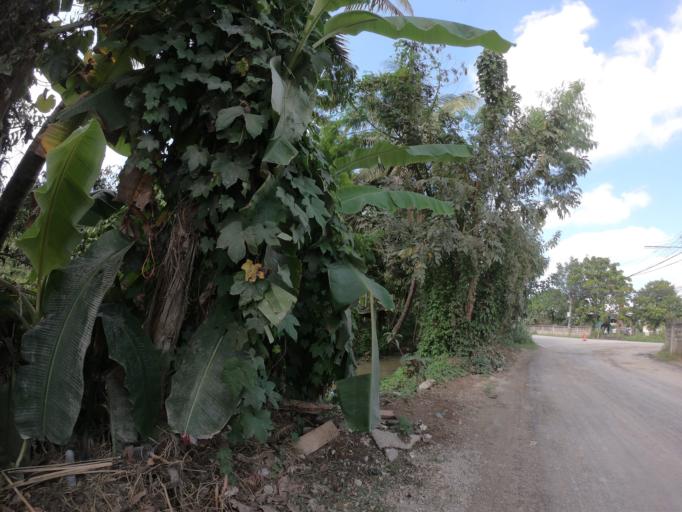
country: TH
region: Chiang Mai
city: San Sai
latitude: 18.8261
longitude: 99.0604
